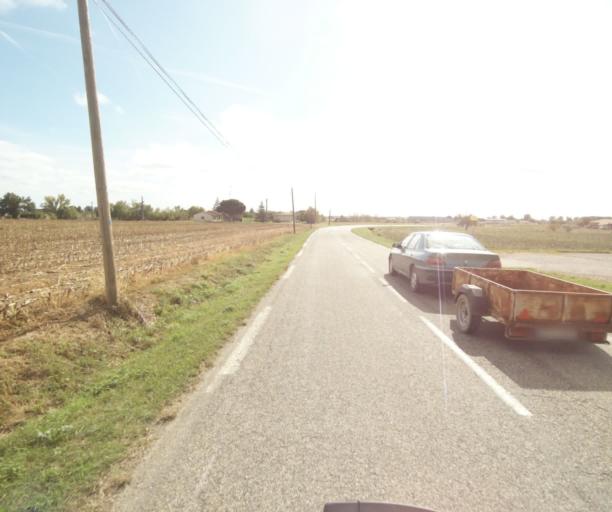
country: FR
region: Midi-Pyrenees
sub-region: Departement du Tarn-et-Garonne
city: Saint-Porquier
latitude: 43.9527
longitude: 1.1608
